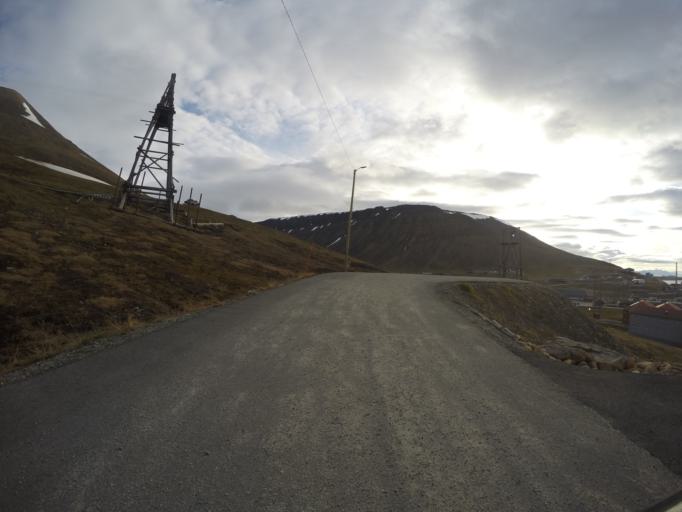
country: SJ
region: Svalbard
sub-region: Spitsbergen
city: Longyearbyen
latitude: 78.2177
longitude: 15.6589
